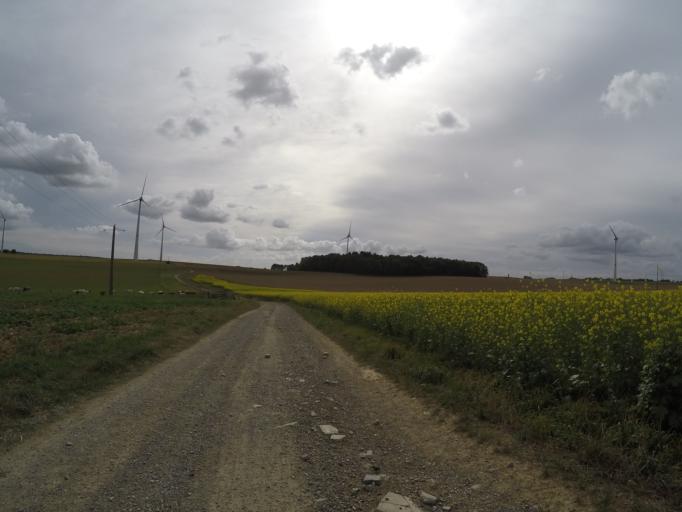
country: BE
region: Wallonia
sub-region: Province de Namur
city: Assesse
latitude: 50.3039
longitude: 4.9809
